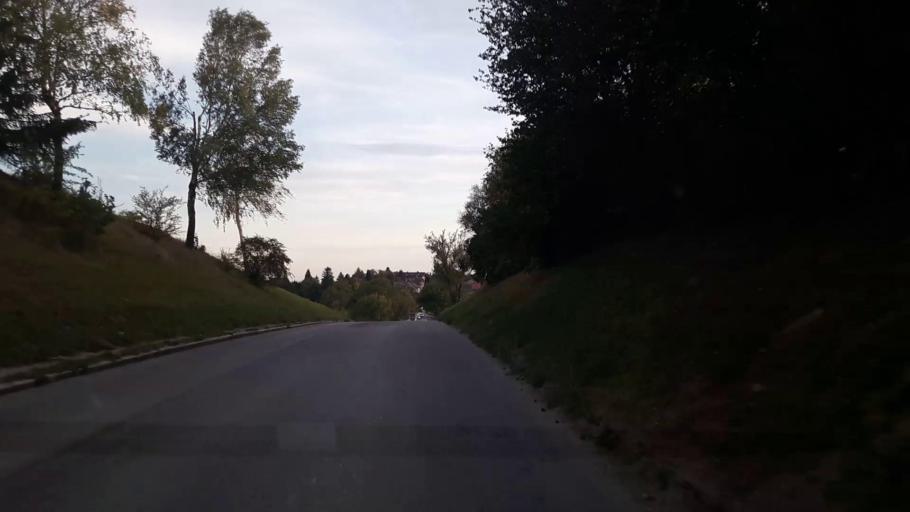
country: AT
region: Lower Austria
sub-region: Politischer Bezirk Korneuburg
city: Ernstbrunn
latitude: 48.5360
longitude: 16.3618
